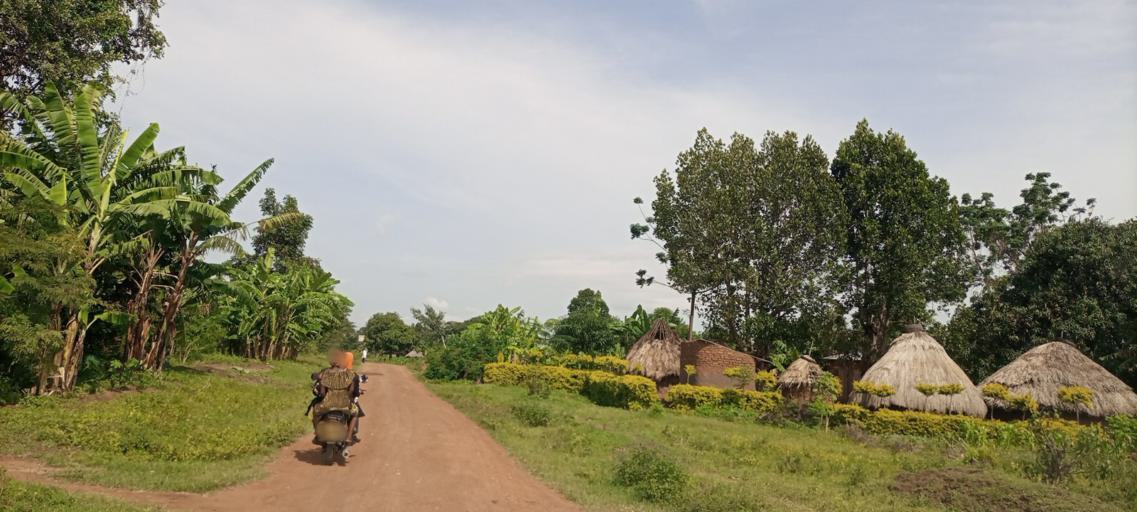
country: UG
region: Eastern Region
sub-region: Mbale District
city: Mbale
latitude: 1.1325
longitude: 34.0498
